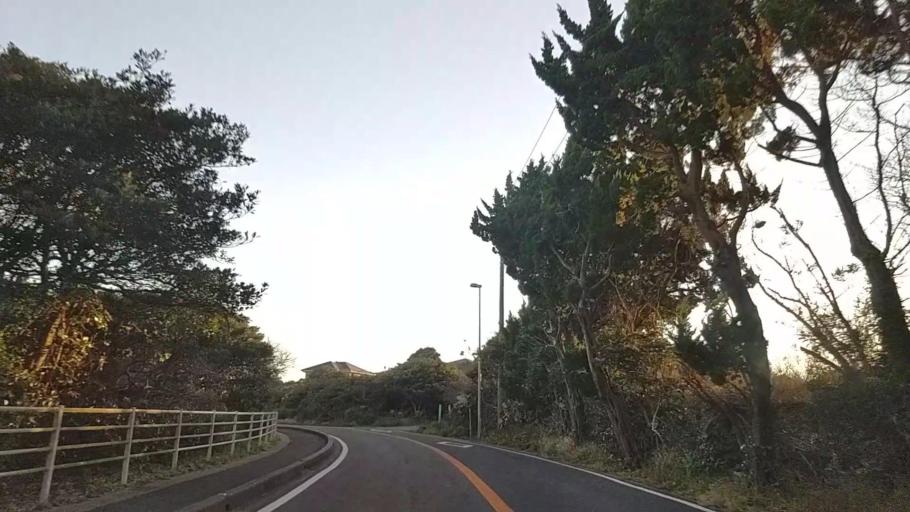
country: JP
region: Chiba
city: Hasaki
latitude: 35.6997
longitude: 140.8616
